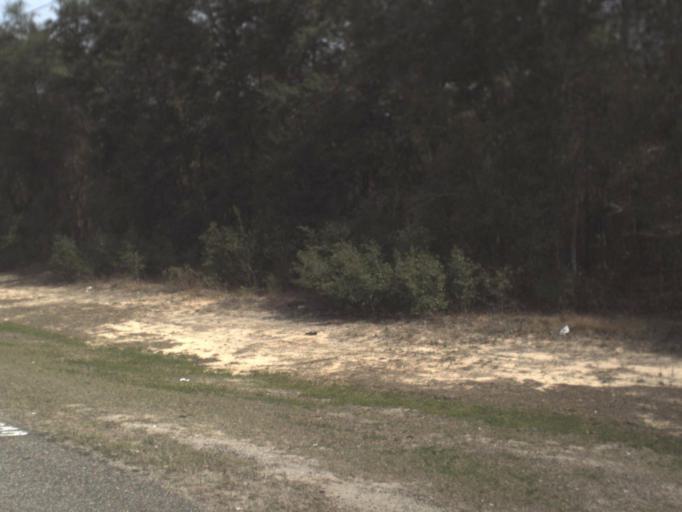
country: US
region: Florida
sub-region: Leon County
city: Tallahassee
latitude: 30.4120
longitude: -84.3530
